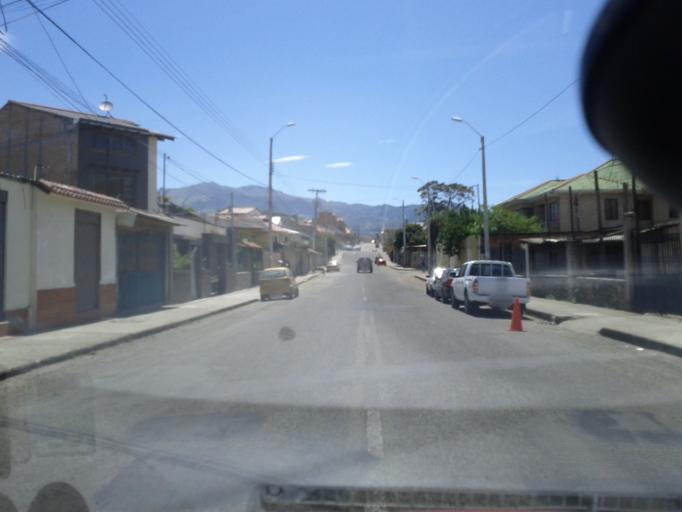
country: EC
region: Azuay
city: Cuenca
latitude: -2.9076
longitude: -79.0149
